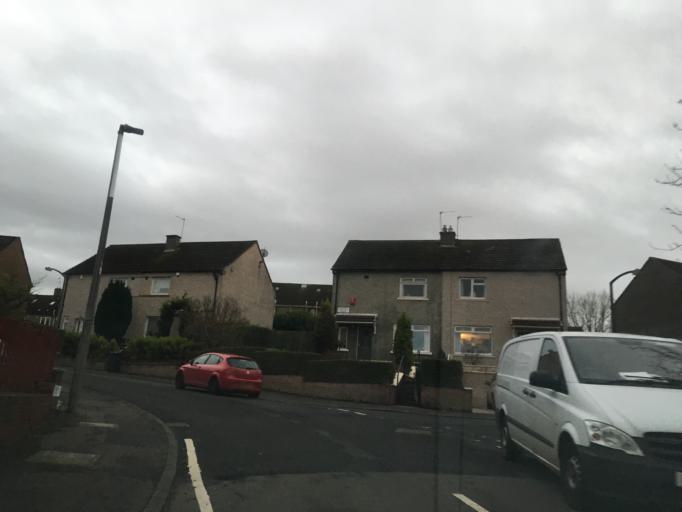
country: GB
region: Scotland
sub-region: Edinburgh
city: Colinton
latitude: 55.9222
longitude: -3.2613
